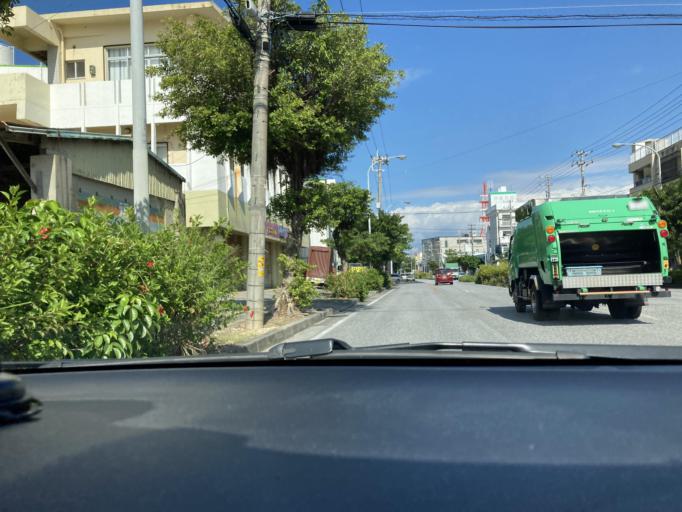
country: JP
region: Okinawa
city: Naha-shi
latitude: 26.2385
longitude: 127.6950
